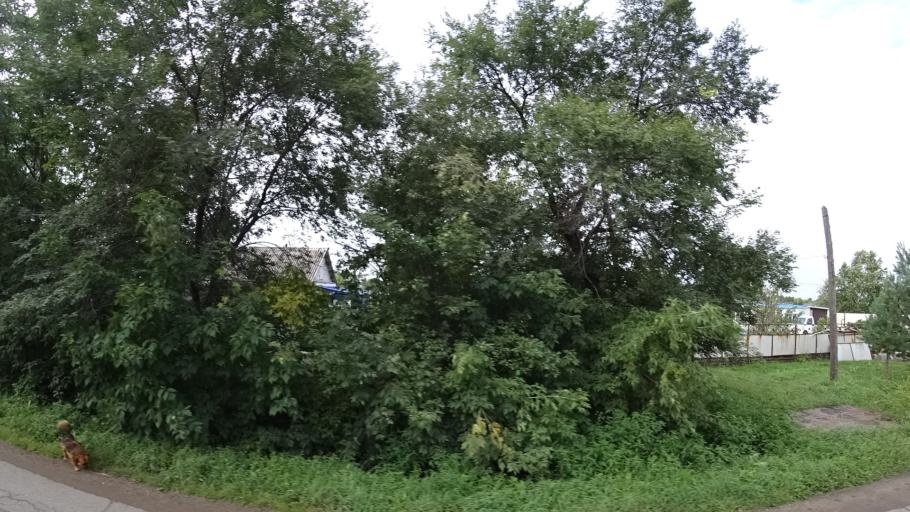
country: RU
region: Primorskiy
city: Chernigovka
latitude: 44.3430
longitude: 132.5669
